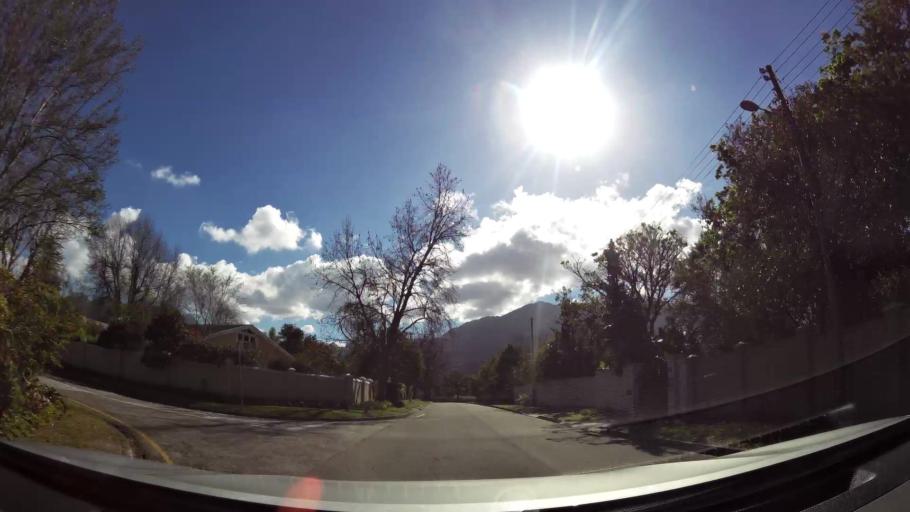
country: ZA
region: Western Cape
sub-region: Eden District Municipality
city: George
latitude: -33.9504
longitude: 22.4409
